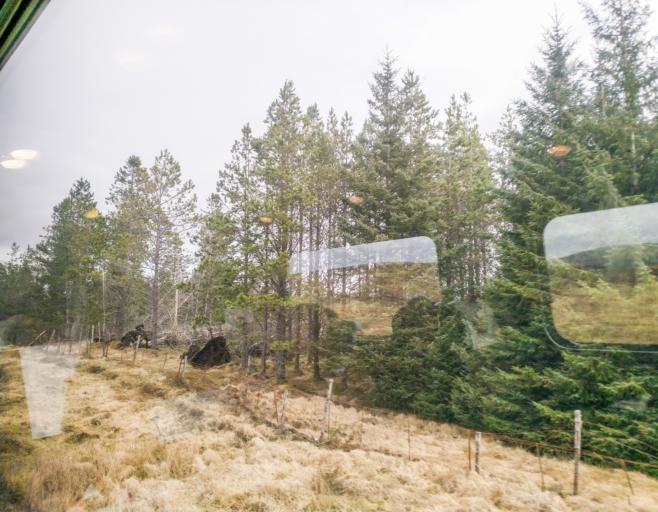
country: GB
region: Scotland
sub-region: Highland
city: Spean Bridge
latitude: 56.6540
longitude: -4.5657
